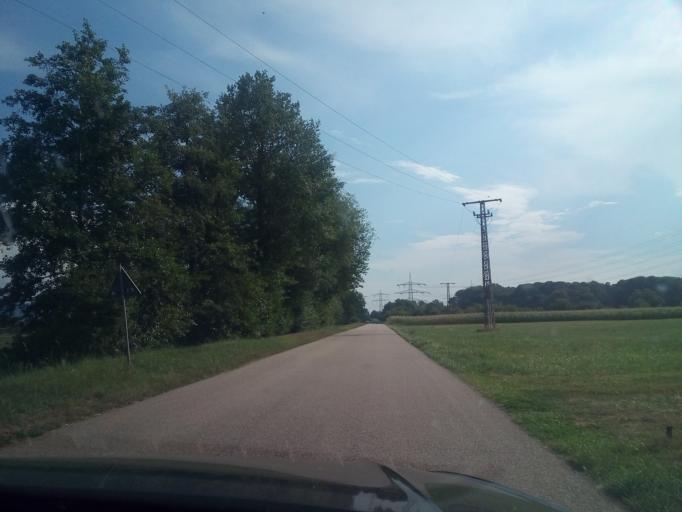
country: DE
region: Baden-Wuerttemberg
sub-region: Karlsruhe Region
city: Ottenhofen
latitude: 48.7558
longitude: 8.1392
